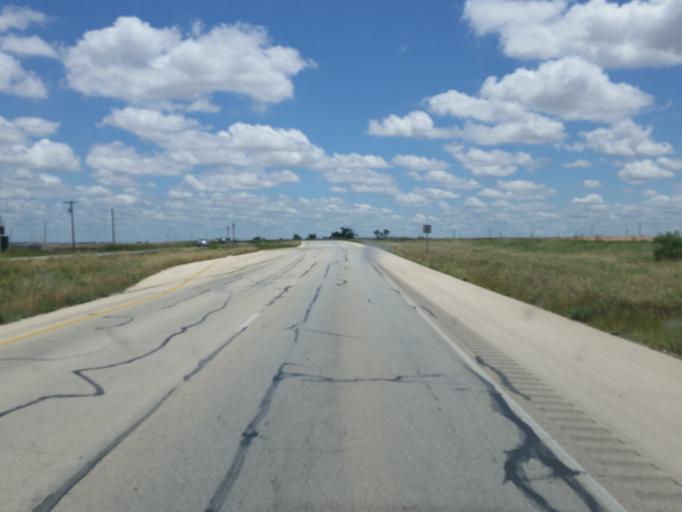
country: US
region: Texas
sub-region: Nolan County
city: Roscoe
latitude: 32.4922
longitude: -100.6341
